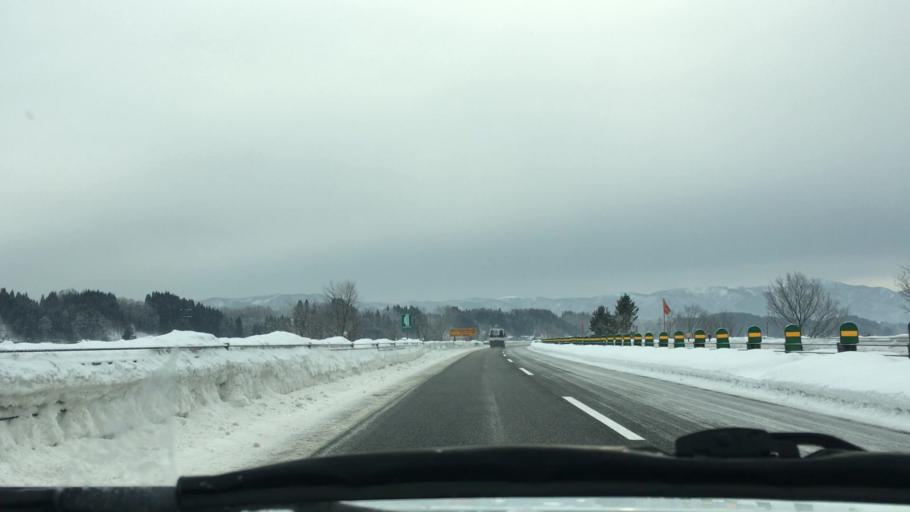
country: JP
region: Akita
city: Hanawa
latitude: 40.2989
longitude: 140.7498
